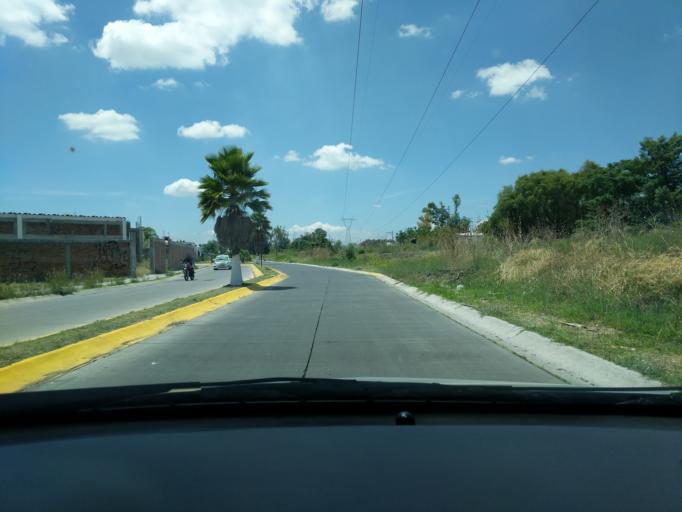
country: MX
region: Guanajuato
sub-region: Salamanca
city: El Divisador
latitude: 20.6008
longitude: -101.1742
